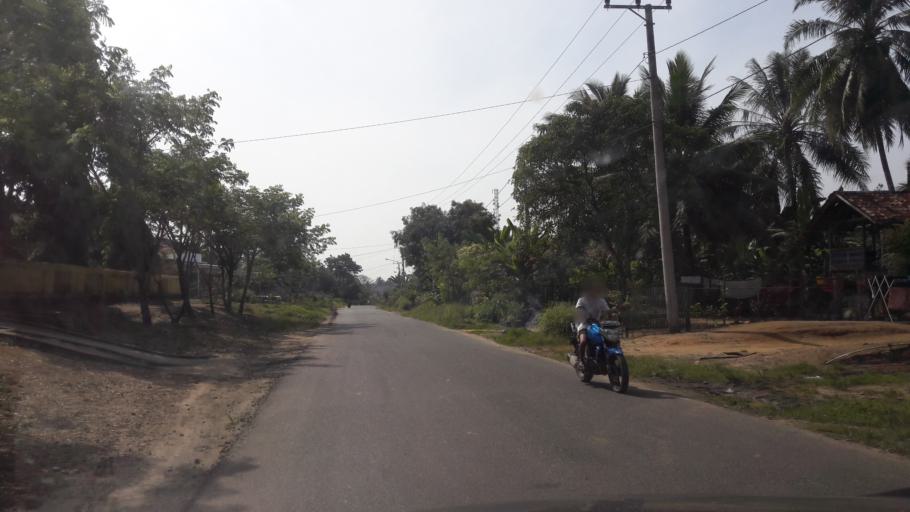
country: ID
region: South Sumatra
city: Gunungmenang
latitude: -3.3285
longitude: 104.0908
